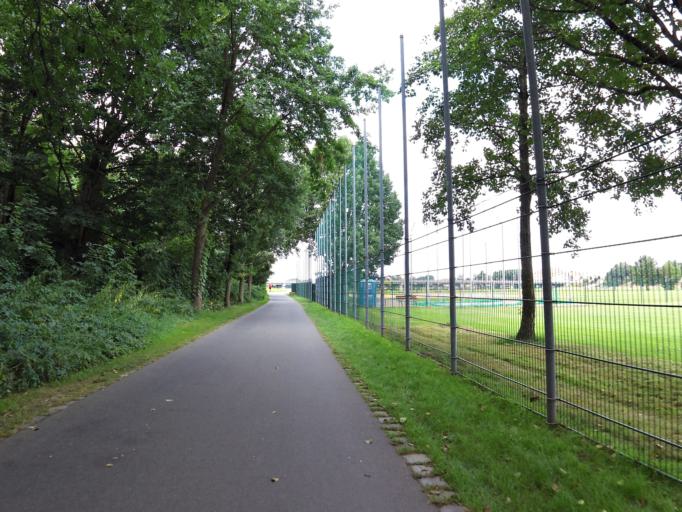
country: DE
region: Saxony
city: Dresden
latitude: 51.0642
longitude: 13.7200
